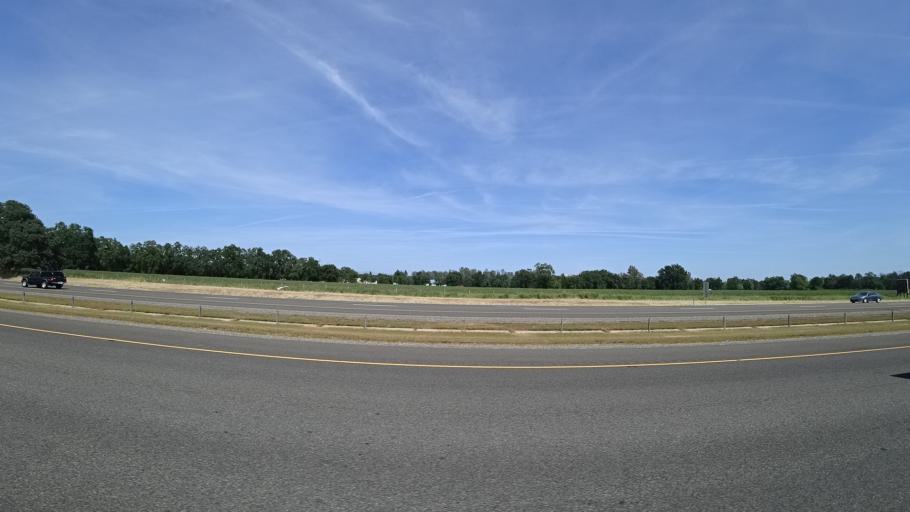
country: US
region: California
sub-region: Shasta County
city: Redding
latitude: 40.5296
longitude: -122.3485
